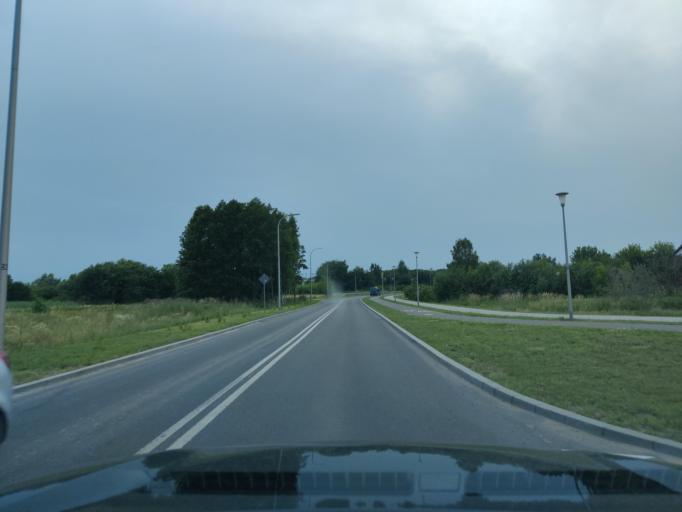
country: PL
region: Masovian Voivodeship
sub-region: Powiat mlawski
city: Mlawa
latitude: 53.1035
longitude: 20.3705
